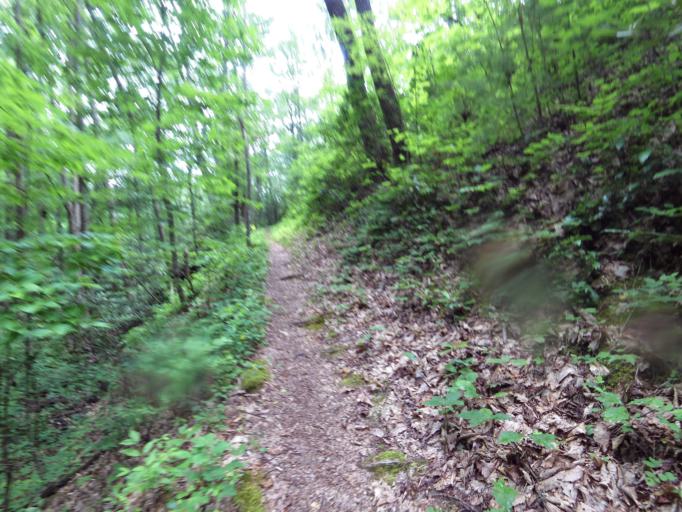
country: US
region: Tennessee
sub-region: Blount County
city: Wildwood
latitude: 35.6498
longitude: -83.8190
